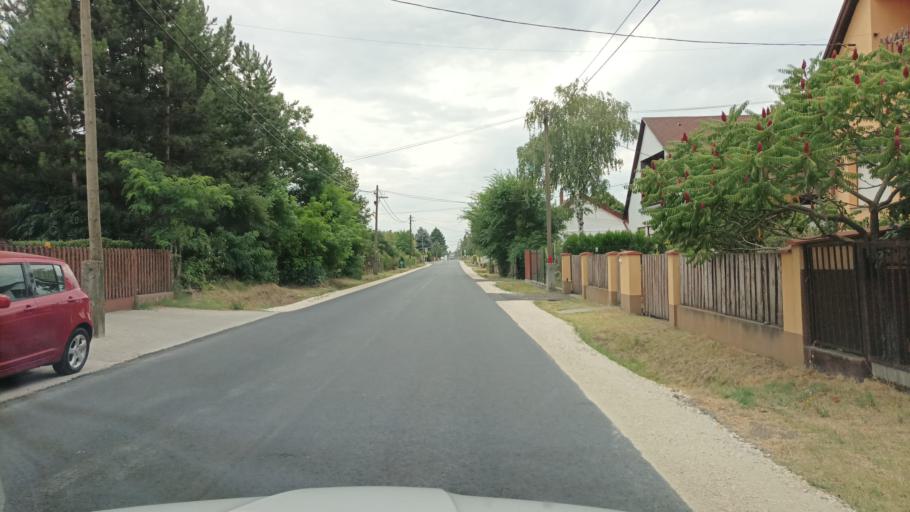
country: HU
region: Pest
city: Taborfalva
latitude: 47.1105
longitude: 19.4906
